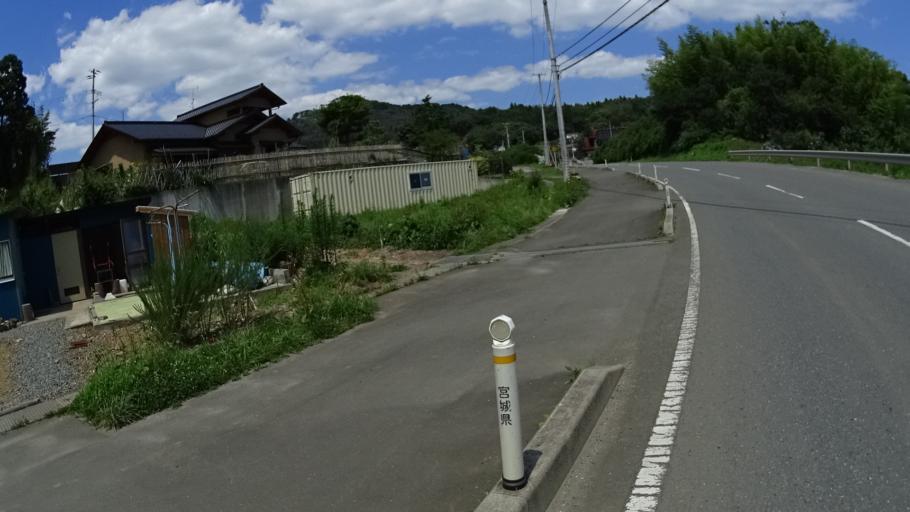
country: JP
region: Iwate
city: Ofunato
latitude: 38.8625
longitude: 141.6178
